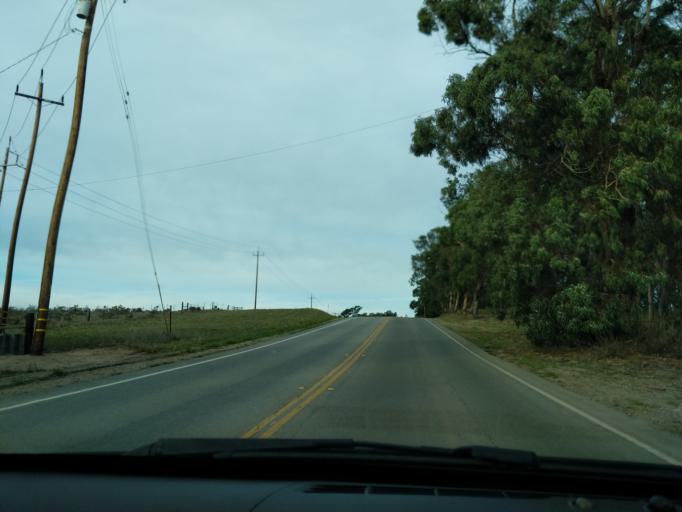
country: US
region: California
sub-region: San Luis Obispo County
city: Callender
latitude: 35.0205
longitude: -120.5635
